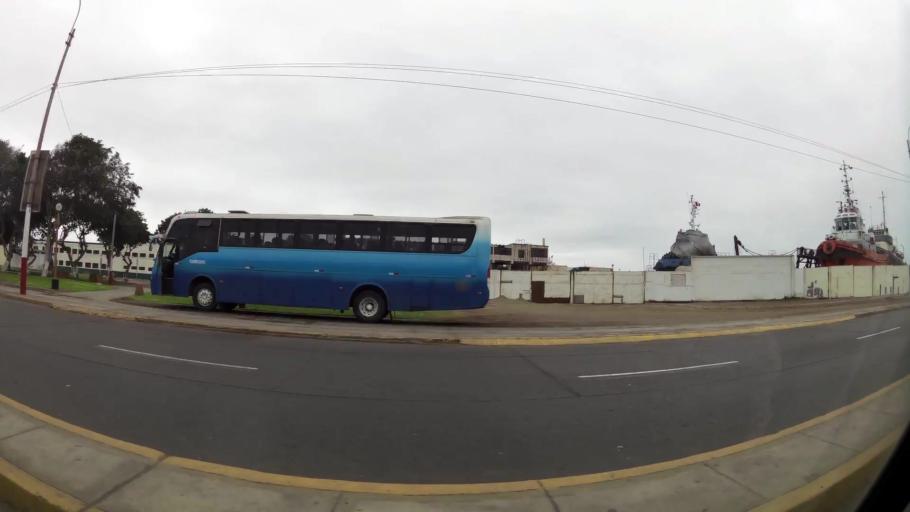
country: PE
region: Callao
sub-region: Callao
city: Callao
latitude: -12.0626
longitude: -77.1512
